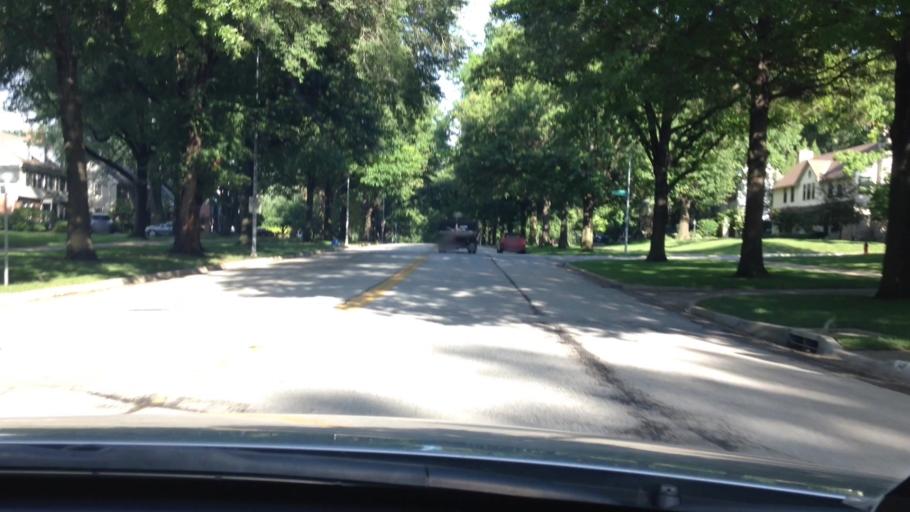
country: US
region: Kansas
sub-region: Johnson County
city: Mission Hills
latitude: 39.0123
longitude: -94.5988
